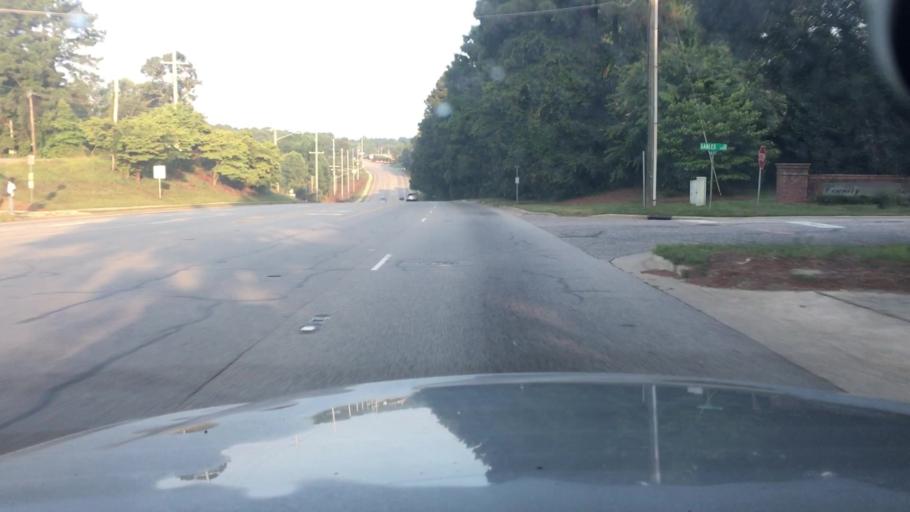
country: US
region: North Carolina
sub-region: Cumberland County
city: Fayetteville
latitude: 35.1043
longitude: -78.8892
